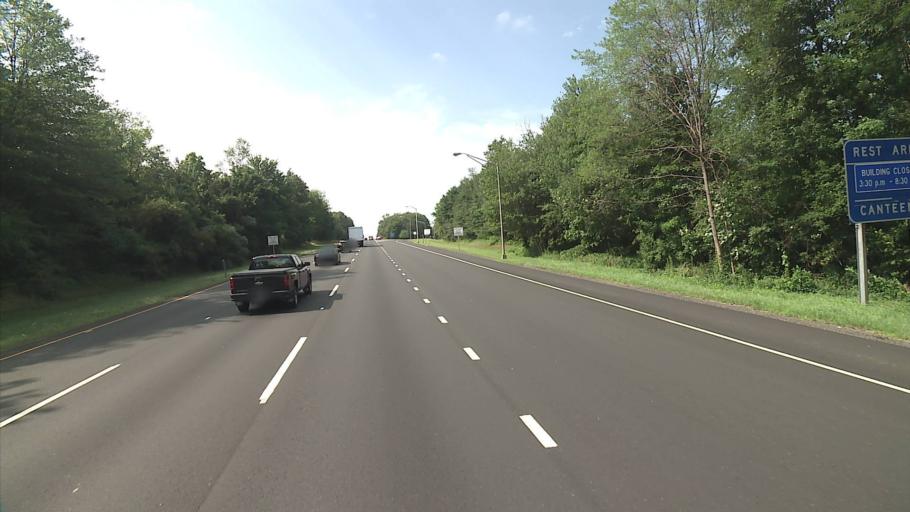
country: US
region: Connecticut
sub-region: New Haven County
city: Wallingford Center
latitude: 41.4652
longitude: -72.7761
